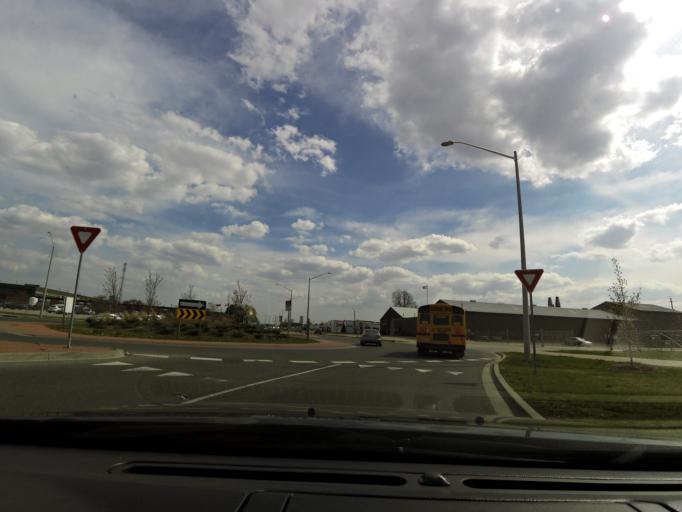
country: CA
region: Ontario
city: Cambridge
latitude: 43.3653
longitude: -80.2926
